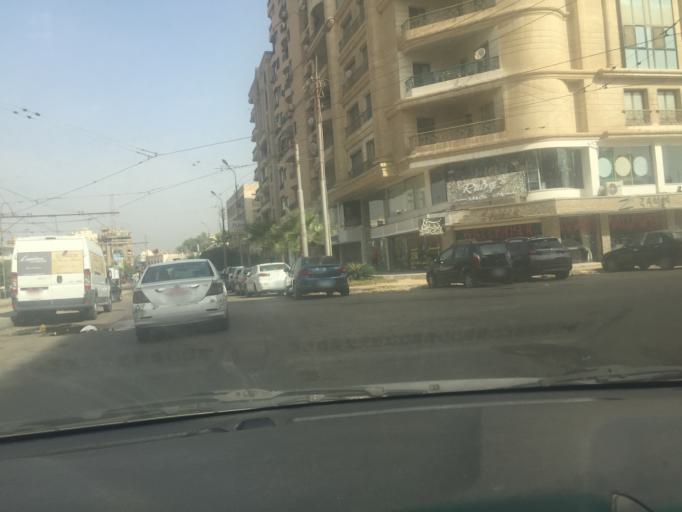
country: EG
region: Muhafazat al Qahirah
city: Cairo
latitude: 30.0838
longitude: 31.3479
